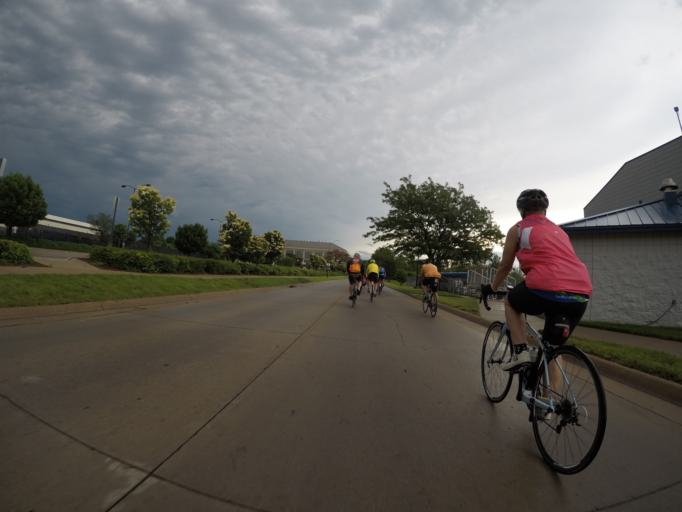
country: US
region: Kansas
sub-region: Shawnee County
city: Topeka
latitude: 39.0320
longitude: -95.7001
